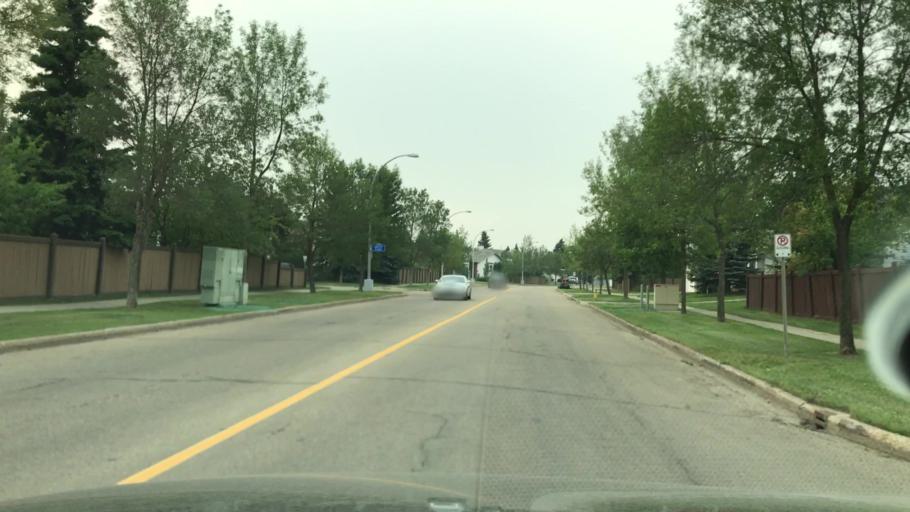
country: CA
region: Alberta
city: Edmonton
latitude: 53.4706
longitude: -113.5718
